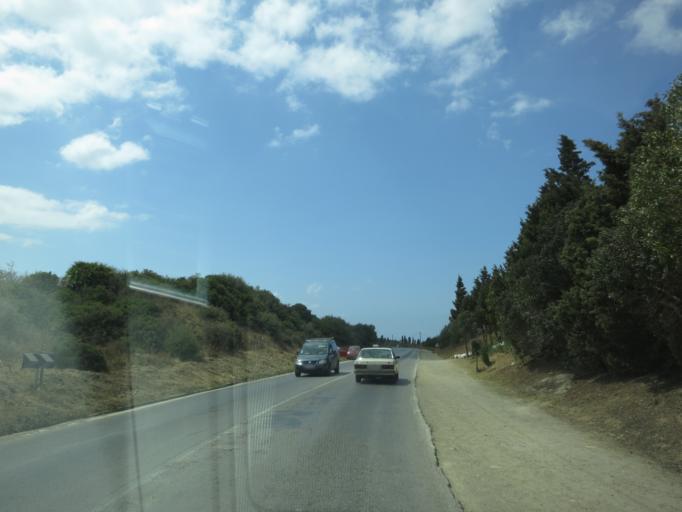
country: MA
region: Tanger-Tetouan
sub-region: Tanger-Assilah
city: Tangier
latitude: 35.8126
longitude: -5.7341
